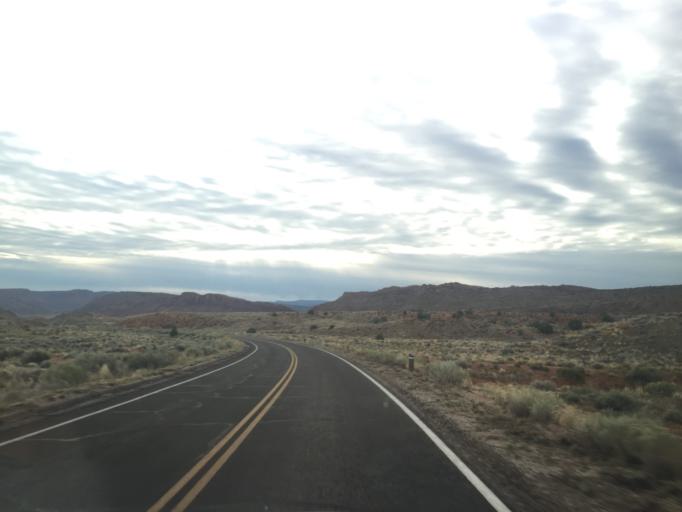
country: US
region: Utah
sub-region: Grand County
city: Moab
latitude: 38.7330
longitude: -109.5562
